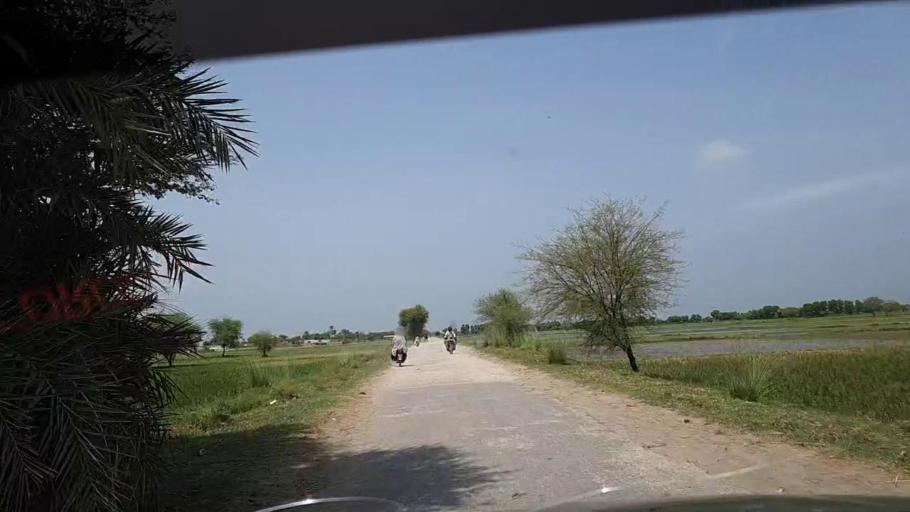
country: PK
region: Sindh
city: Khanpur
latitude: 27.8196
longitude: 69.4445
